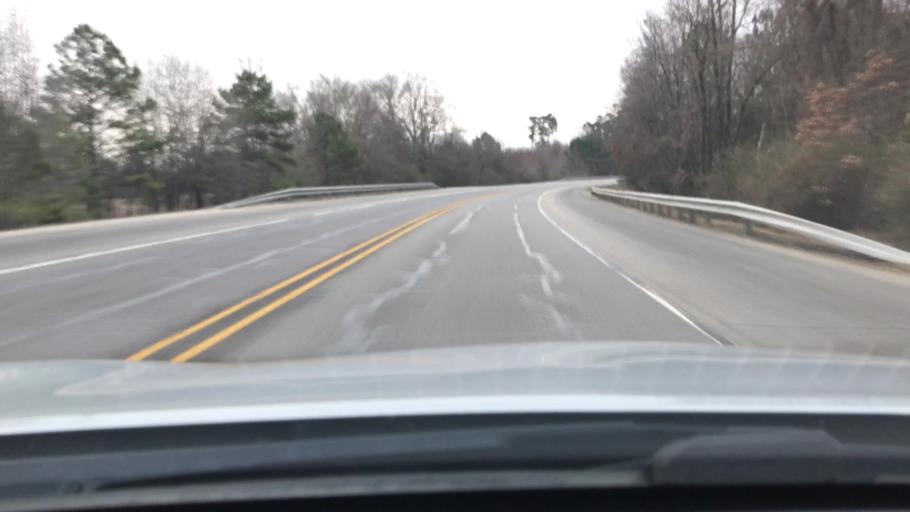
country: US
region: Arkansas
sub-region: Hempstead County
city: Hope
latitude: 33.6851
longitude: -93.5764
